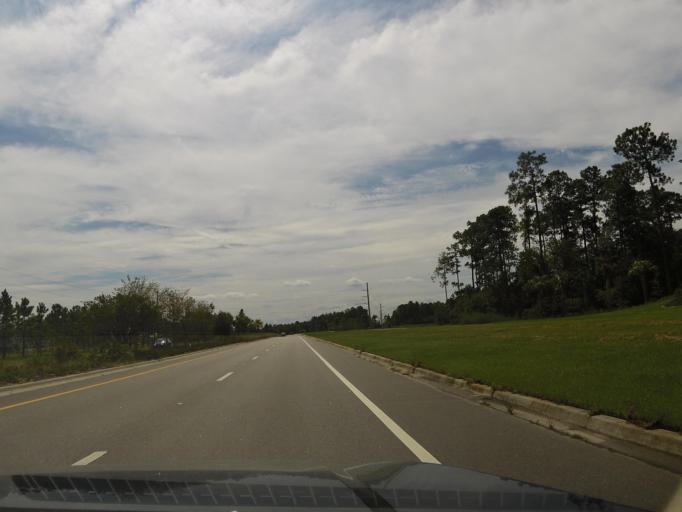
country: US
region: Florida
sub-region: Saint Johns County
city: Fruit Cove
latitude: 30.0385
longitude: -81.5287
